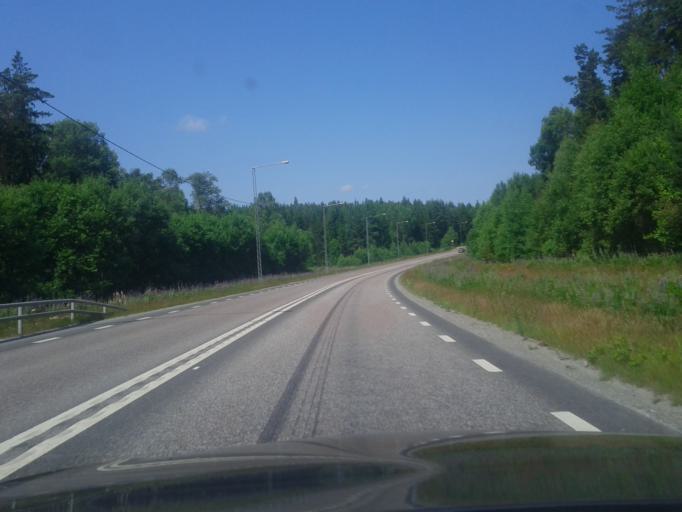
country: SE
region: Stockholm
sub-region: Vallentuna Kommun
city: Vallentuna
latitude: 59.4961
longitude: 18.1032
